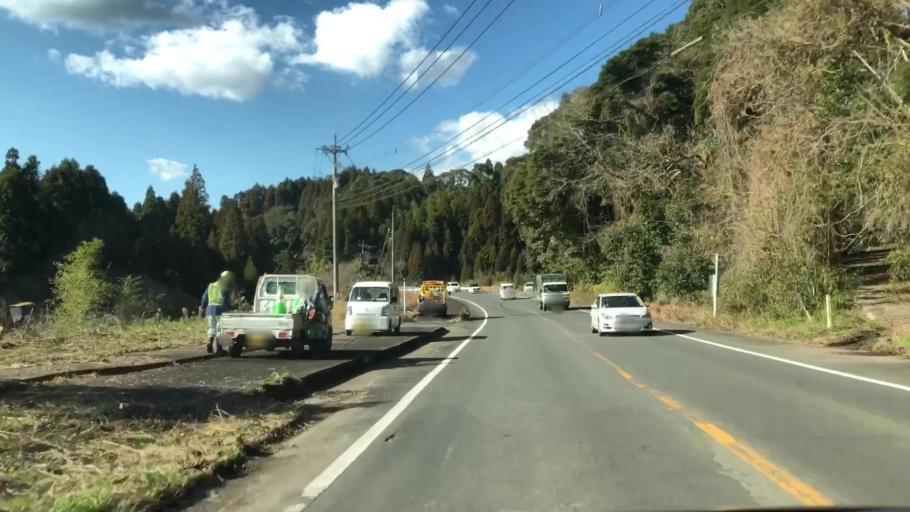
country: JP
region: Kagoshima
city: Satsumasendai
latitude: 31.8613
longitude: 130.4025
